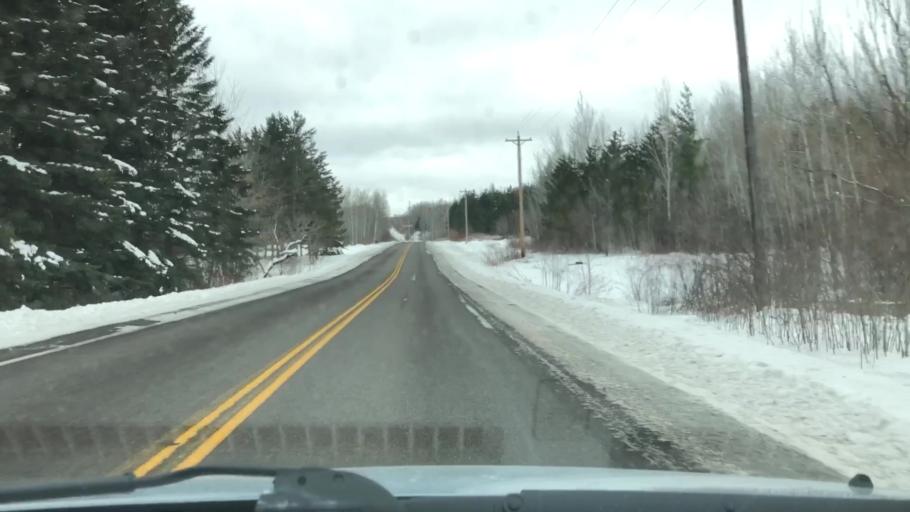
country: US
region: Minnesota
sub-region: Saint Louis County
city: Proctor
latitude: 46.6997
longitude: -92.2812
